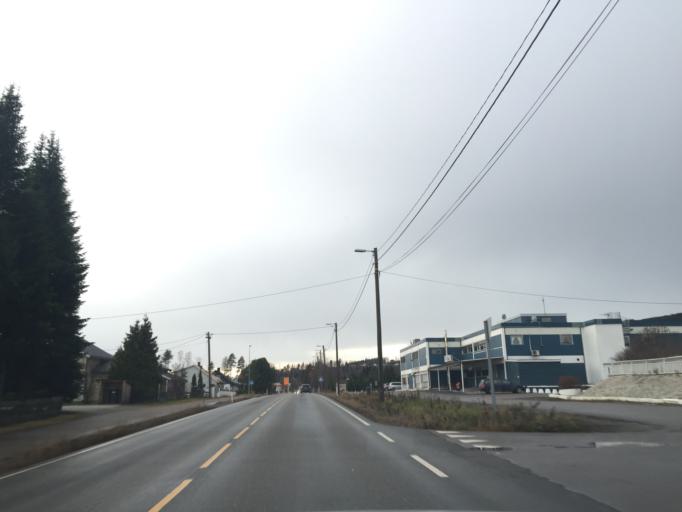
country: NO
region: Hedmark
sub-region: Asnes
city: Flisa
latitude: 60.6132
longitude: 12.0242
